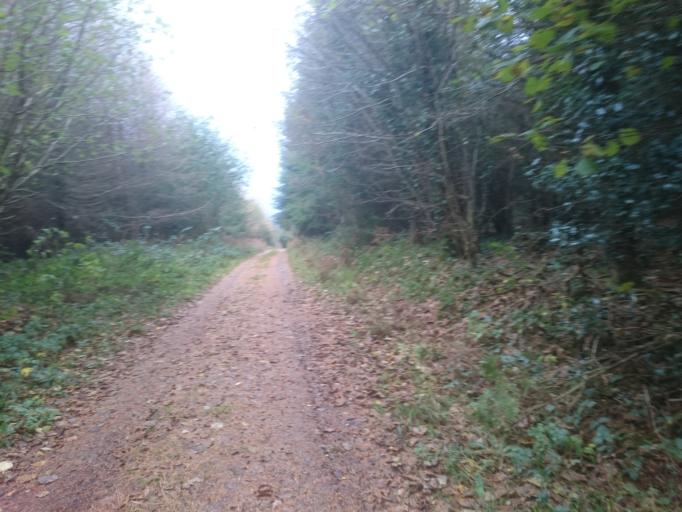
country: IE
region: Leinster
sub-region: Kilkenny
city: Thomastown
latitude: 52.4668
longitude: -7.0499
